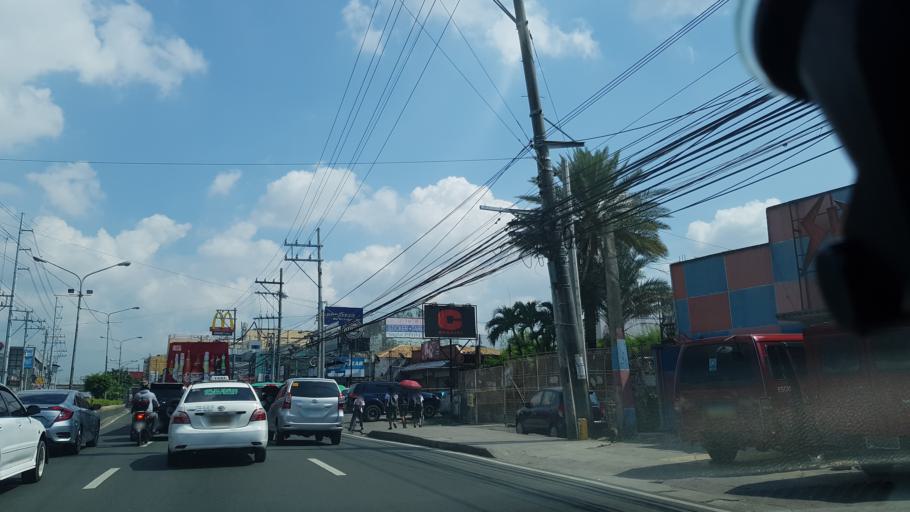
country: PH
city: Sambayanihan People's Village
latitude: 14.4772
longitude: 120.9991
